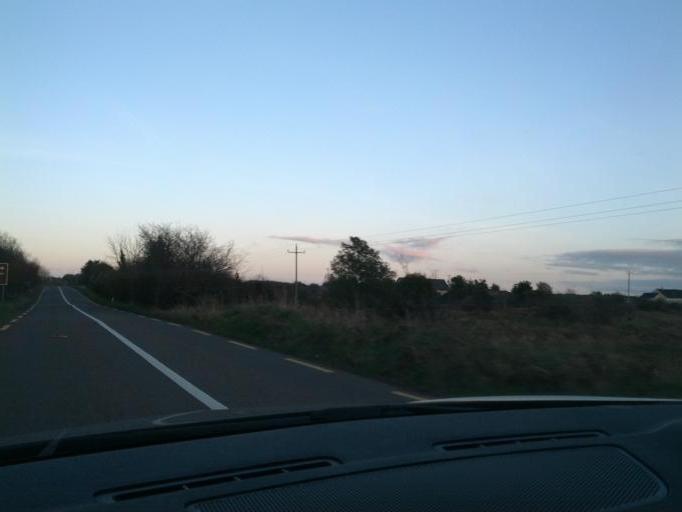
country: IE
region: Connaught
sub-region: Sligo
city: Ballymote
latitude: 53.9738
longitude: -8.4376
